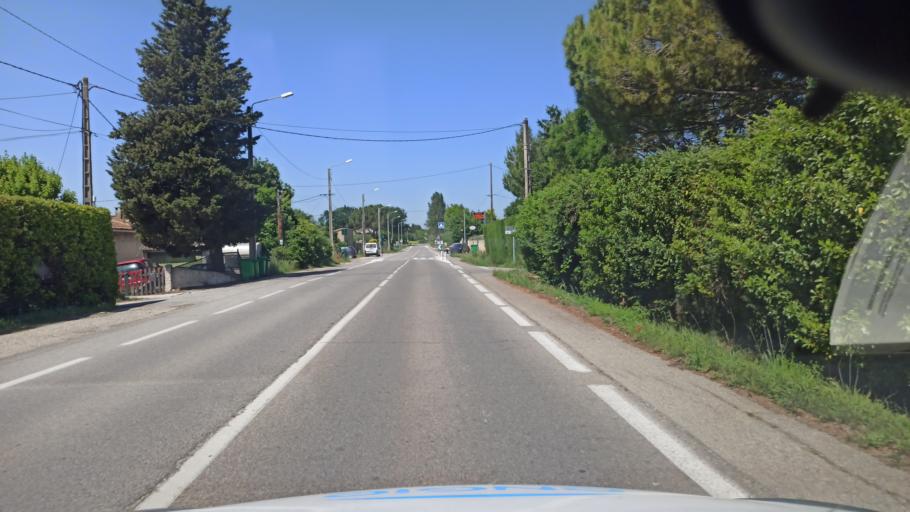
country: FR
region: Provence-Alpes-Cote d'Azur
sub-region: Departement du Vaucluse
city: Morieres-les-Avignon
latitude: 43.9494
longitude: 4.8925
